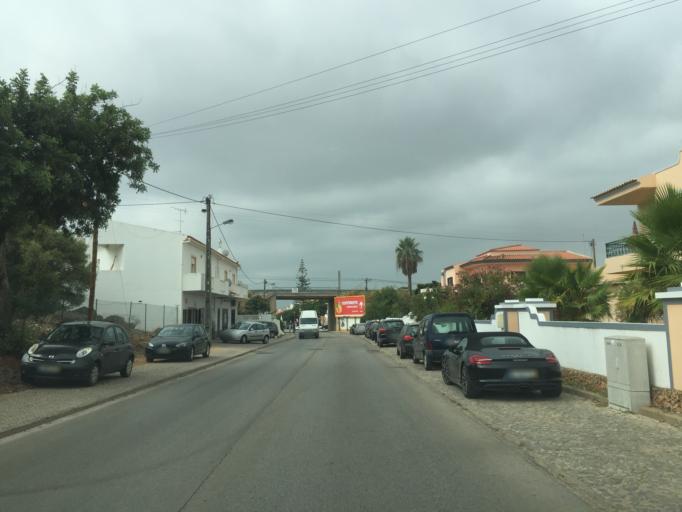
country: PT
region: Faro
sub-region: Loule
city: Almancil
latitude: 37.0937
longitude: -8.0255
